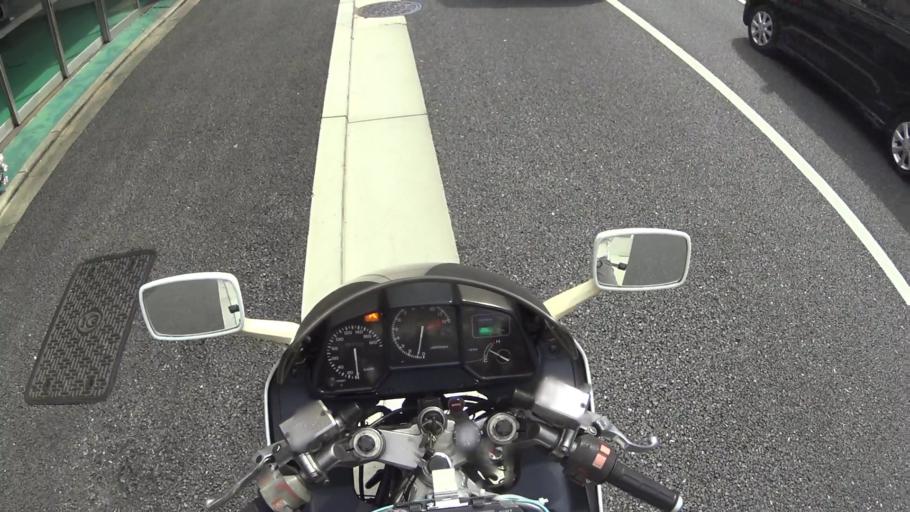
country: JP
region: Kyoto
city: Kyoto
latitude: 35.0003
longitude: 135.7487
